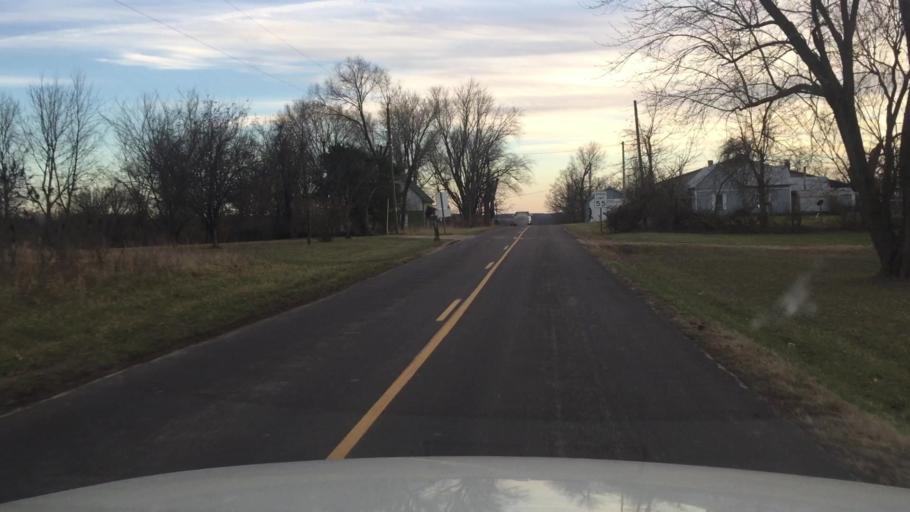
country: US
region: Missouri
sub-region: Miller County
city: Eldon
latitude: 38.3744
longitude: -92.6793
